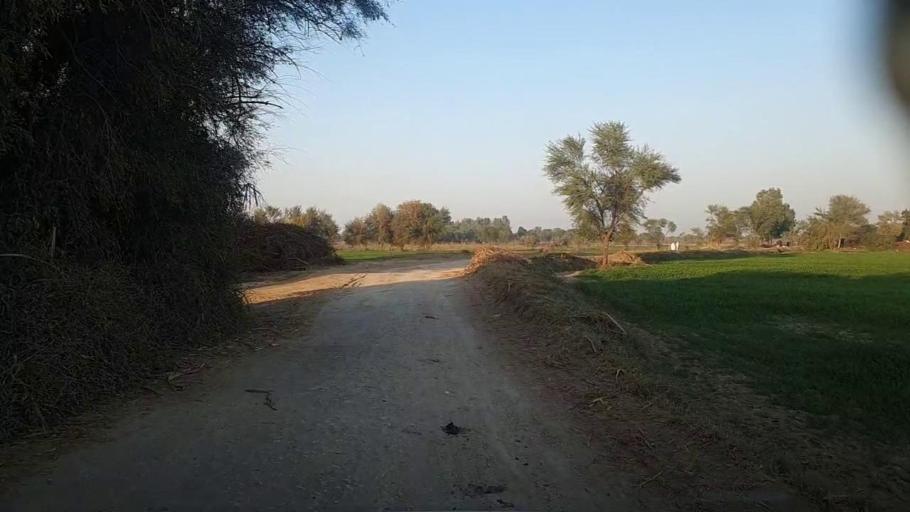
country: PK
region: Sindh
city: Mirpur Mathelo
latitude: 27.8884
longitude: 69.6550
